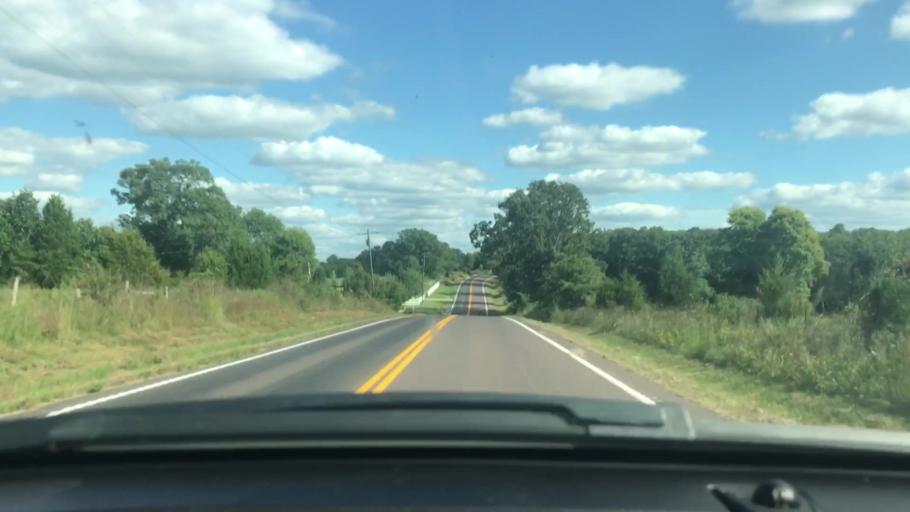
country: US
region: Missouri
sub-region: Wright County
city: Mountain Grove
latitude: 37.2325
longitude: -92.2975
